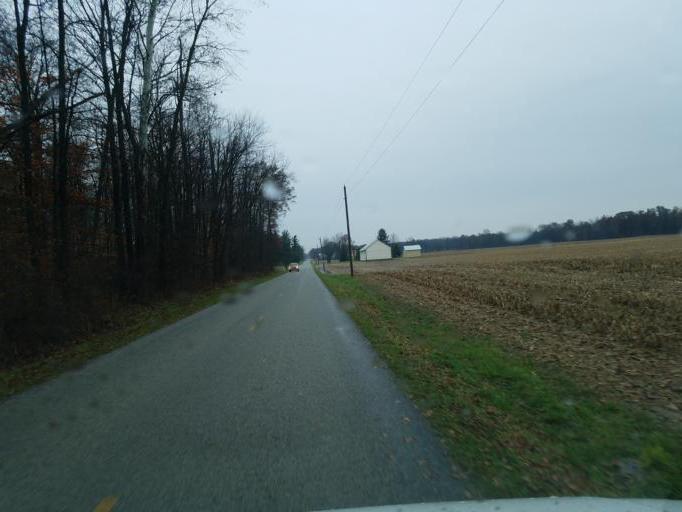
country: US
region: Ohio
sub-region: Knox County
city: Centerburg
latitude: 40.3002
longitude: -82.7729
